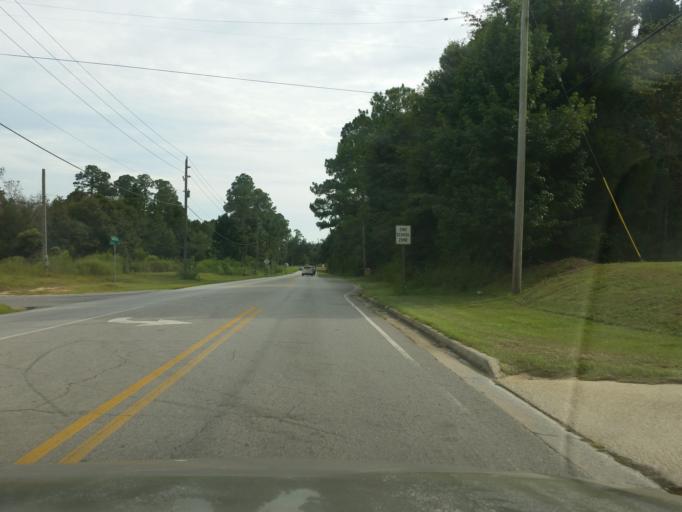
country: US
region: Florida
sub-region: Escambia County
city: Cantonment
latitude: 30.6237
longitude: -87.3226
